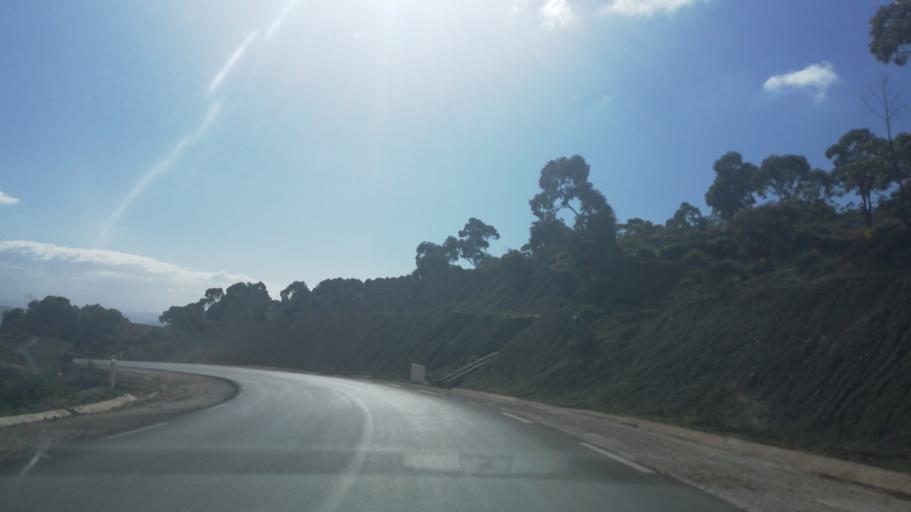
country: DZ
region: Relizane
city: Djidiouia
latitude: 36.0957
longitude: 0.5202
